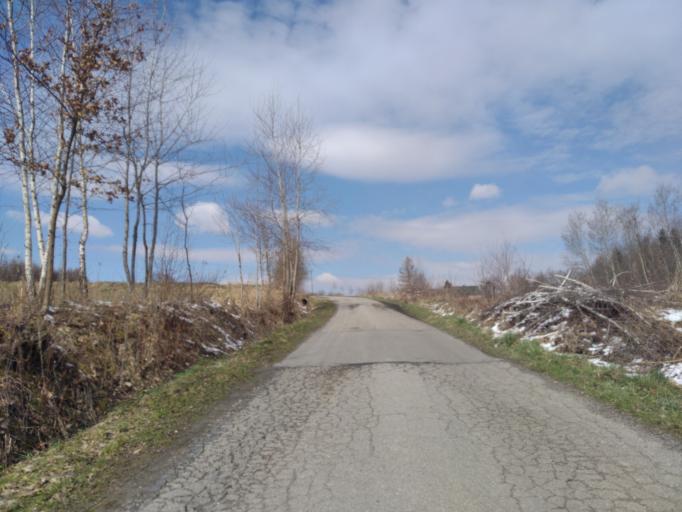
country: PL
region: Subcarpathian Voivodeship
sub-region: Powiat ropczycko-sedziszowski
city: Ropczyce
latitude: 50.0046
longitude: 21.5957
